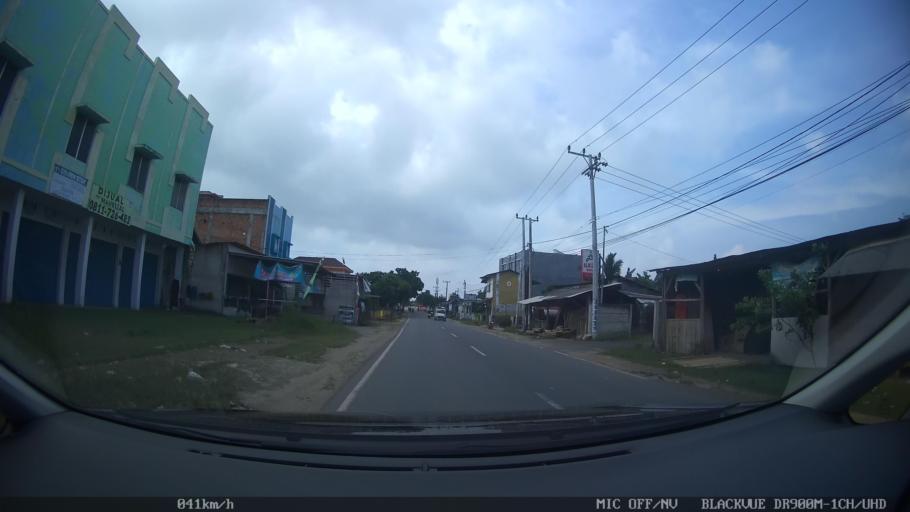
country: ID
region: Lampung
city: Kedaton
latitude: -5.3279
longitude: 105.2902
